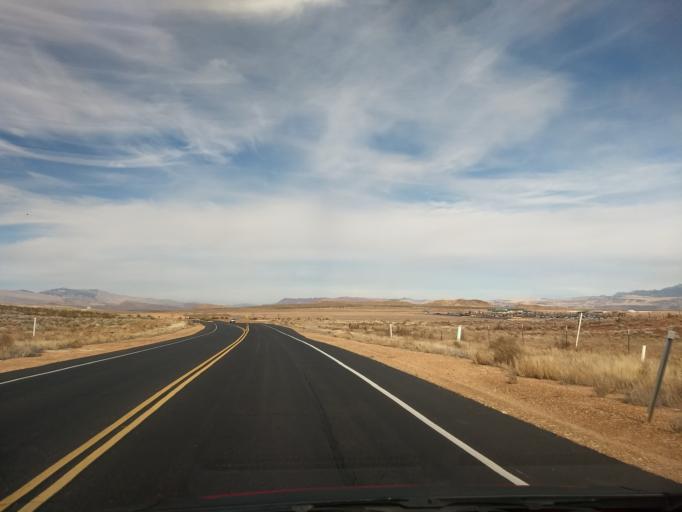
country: US
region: Utah
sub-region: Washington County
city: Washington
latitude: 37.0223
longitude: -113.5047
